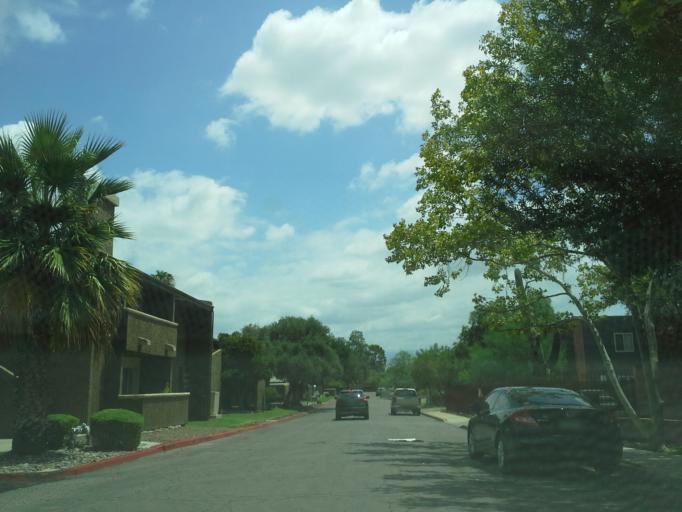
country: US
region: Arizona
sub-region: Pima County
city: Tucson
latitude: 32.2312
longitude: -110.9260
